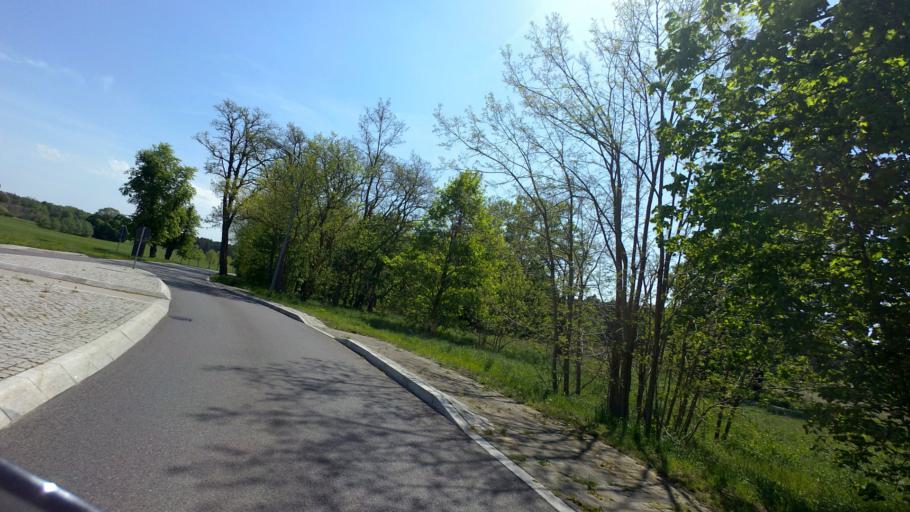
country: DE
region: Brandenburg
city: Neu Zauche
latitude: 52.0343
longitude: 14.0384
